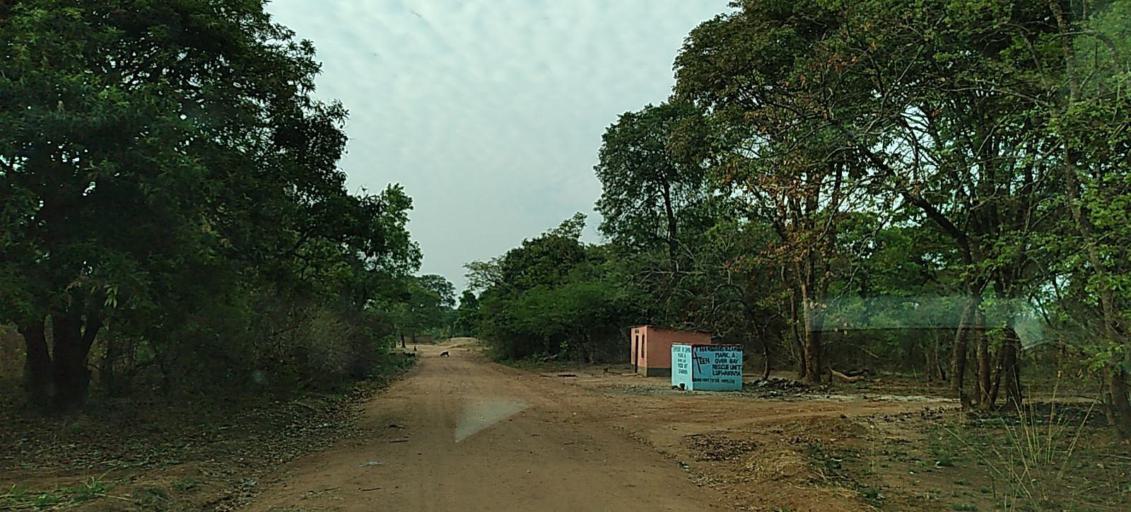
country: ZM
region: Copperbelt
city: Kalulushi
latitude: -12.9094
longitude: 27.6892
